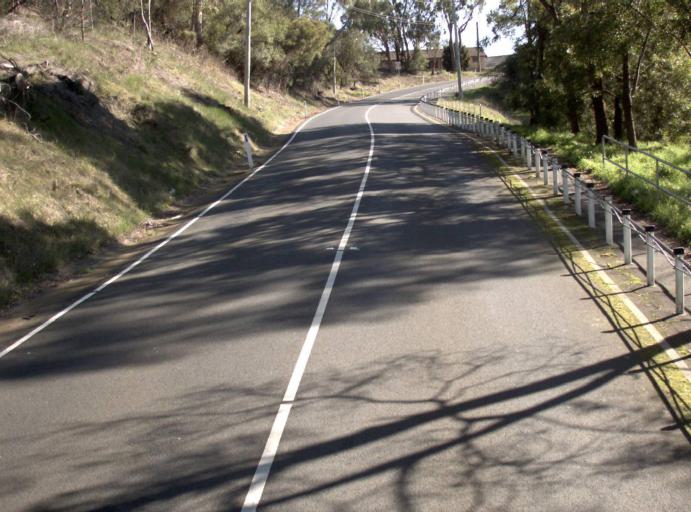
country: AU
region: Tasmania
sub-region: Launceston
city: East Launceston
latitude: -41.4556
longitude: 147.1643
